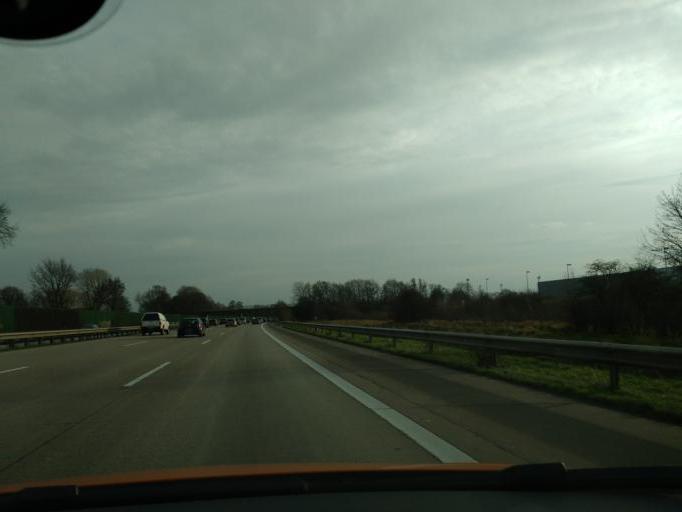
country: DE
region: Lower Saxony
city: Riede
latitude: 53.0375
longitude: 8.9075
